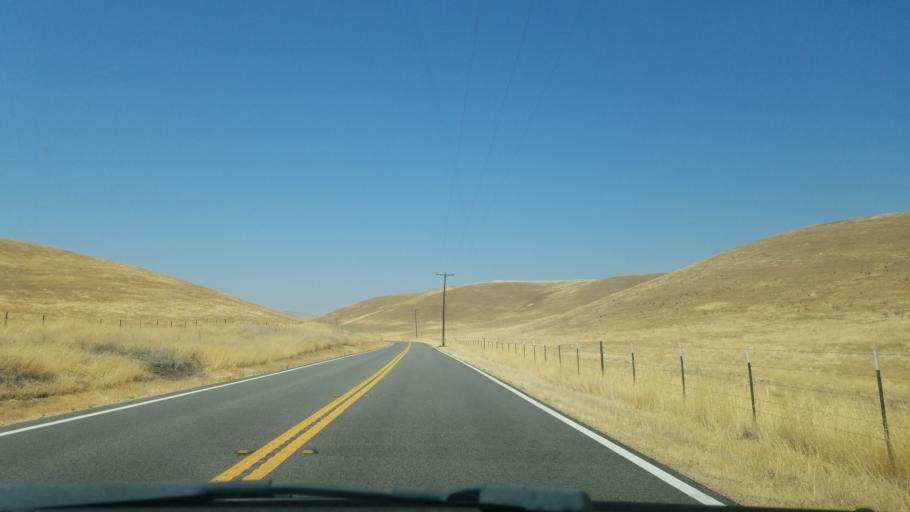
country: US
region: California
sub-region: San Luis Obispo County
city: Shandon
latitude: 35.6054
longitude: -120.4086
